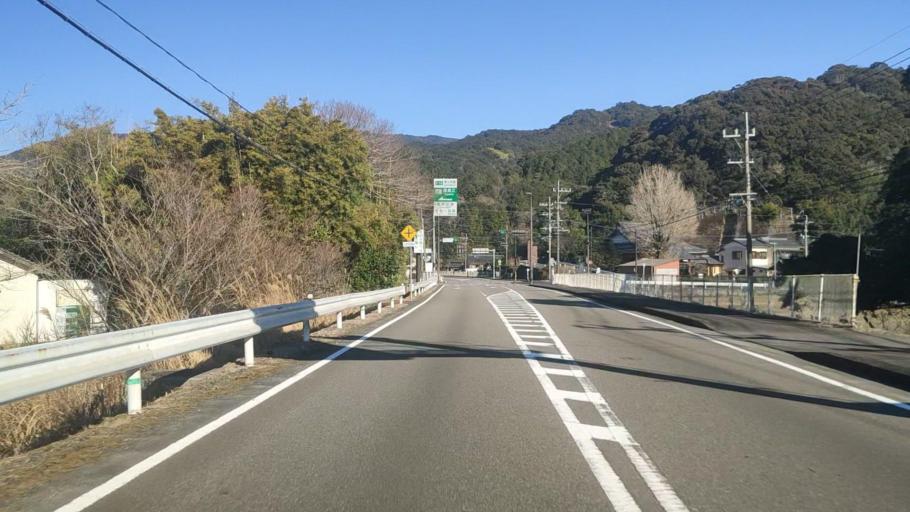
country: JP
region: Miyazaki
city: Nobeoka
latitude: 32.6646
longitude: 131.7667
